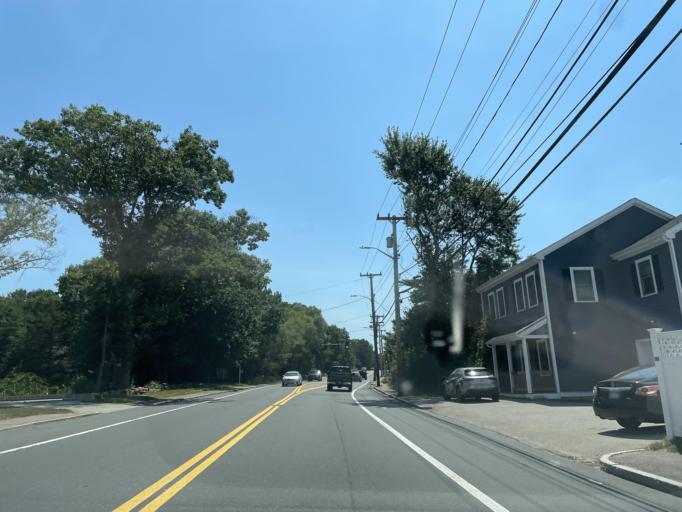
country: US
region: Massachusetts
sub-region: Norfolk County
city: Braintree
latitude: 42.1894
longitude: -71.0073
